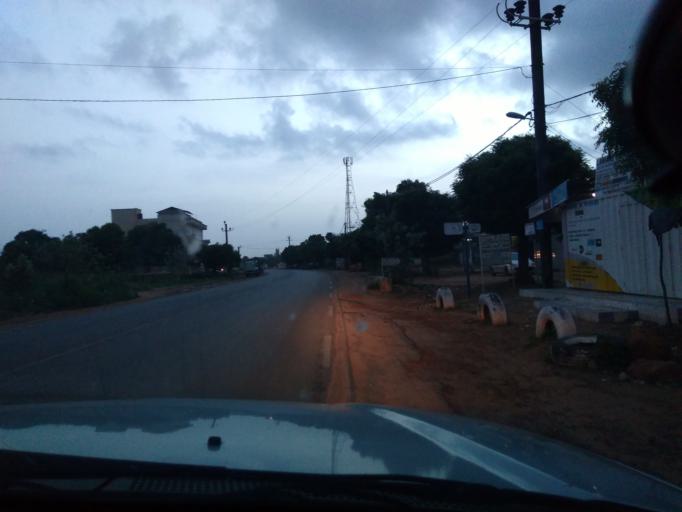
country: SN
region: Thies
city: Pout
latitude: 14.7411
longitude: -17.1387
